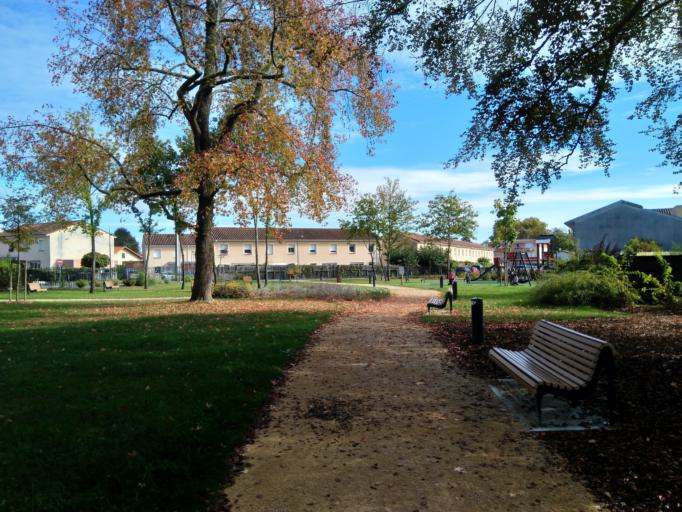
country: FR
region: Aquitaine
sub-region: Departement des Landes
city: Saint-Paul-les-Dax
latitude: 43.7248
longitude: -1.0559
